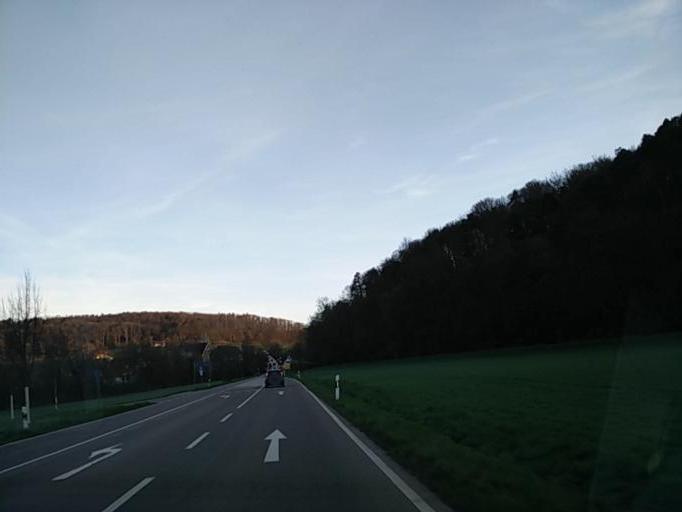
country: DE
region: Baden-Wuerttemberg
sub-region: Tuebingen Region
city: Tuebingen
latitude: 48.5576
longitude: 9.0653
